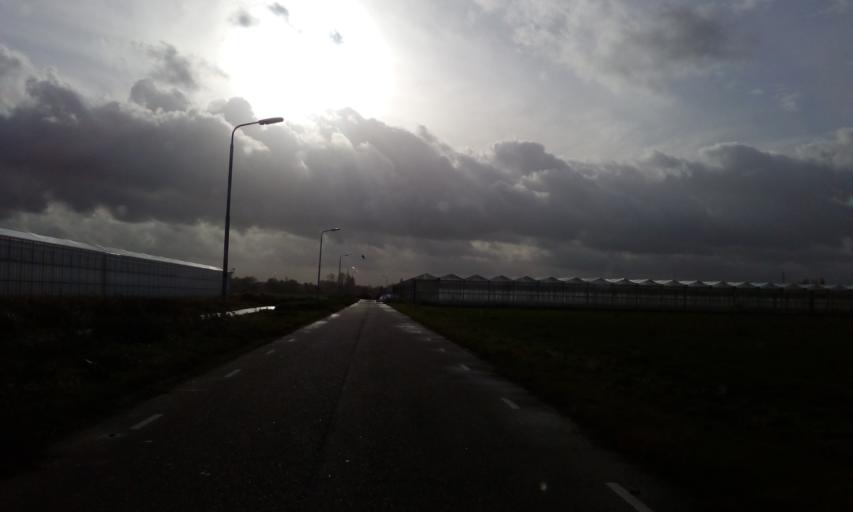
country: NL
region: South Holland
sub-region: Gemeente Lansingerland
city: Berkel en Rodenrijs
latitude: 52.0143
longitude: 4.4908
